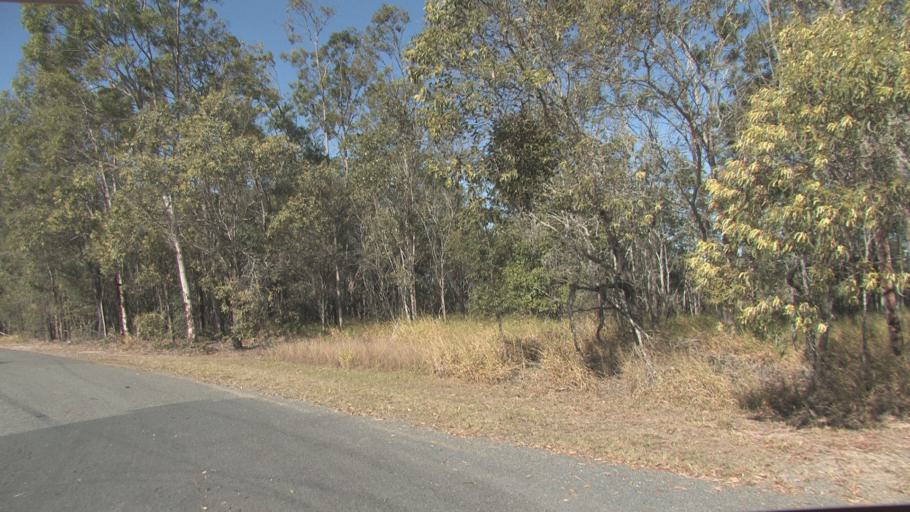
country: AU
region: Queensland
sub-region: Ipswich
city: Springfield Lakes
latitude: -27.7208
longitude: 152.9369
